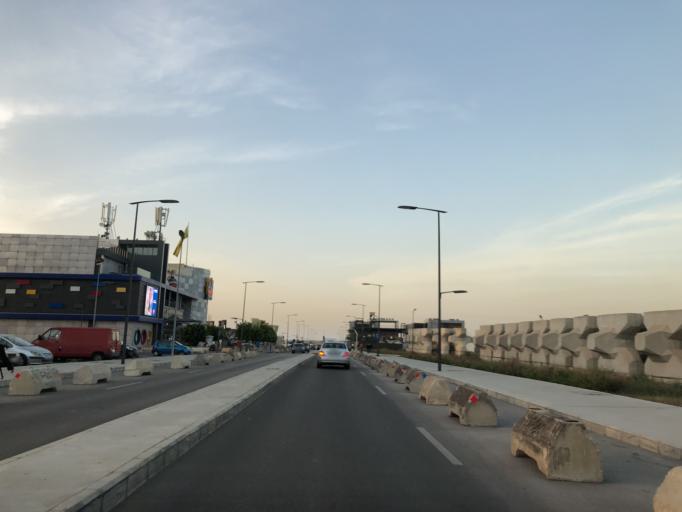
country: LB
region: Beyrouth
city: Beirut
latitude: 33.9038
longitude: 35.5058
